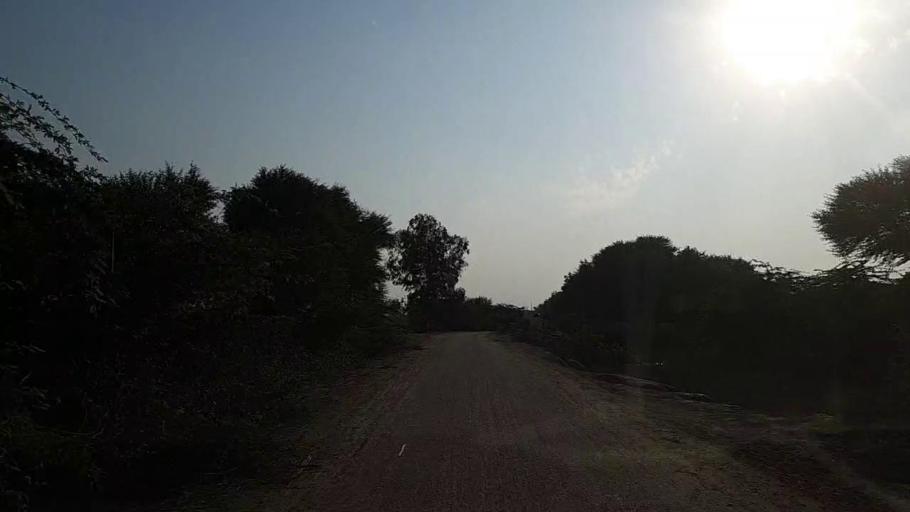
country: PK
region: Sindh
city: Mirpur Batoro
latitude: 24.7772
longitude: 68.2403
